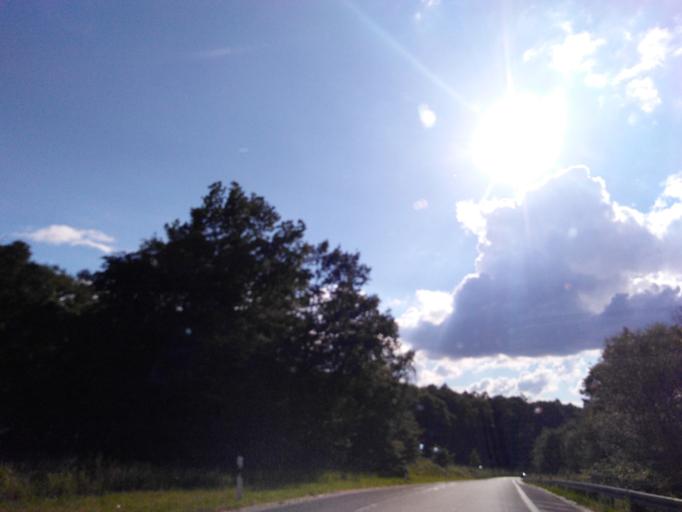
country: DE
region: North Rhine-Westphalia
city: Herdecke
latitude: 51.4421
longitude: 7.4833
